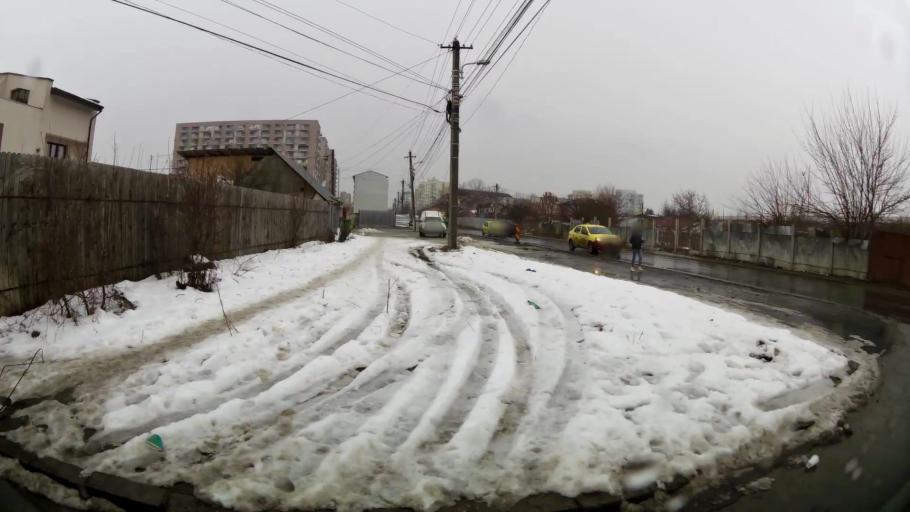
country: RO
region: Ilfov
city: Dobroesti
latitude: 44.4221
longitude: 26.1839
